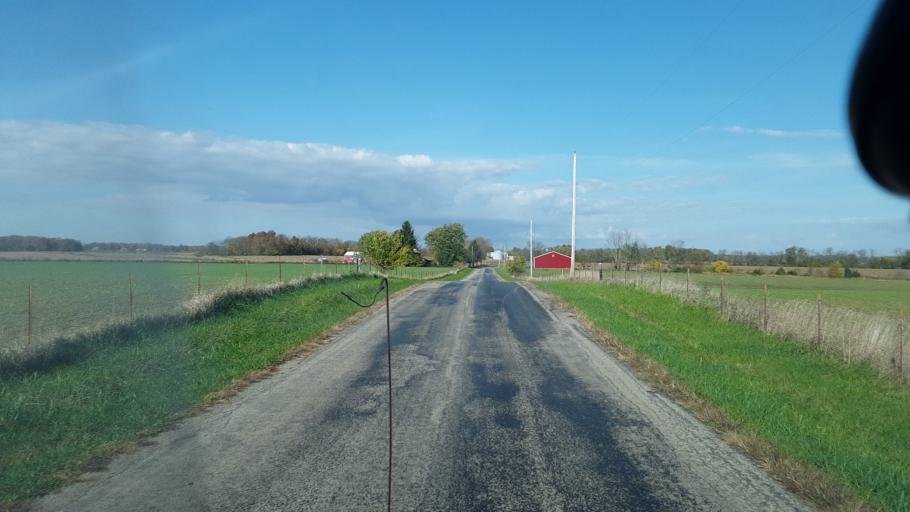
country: US
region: Ohio
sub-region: Highland County
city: Leesburg
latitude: 39.2780
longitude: -83.5675
